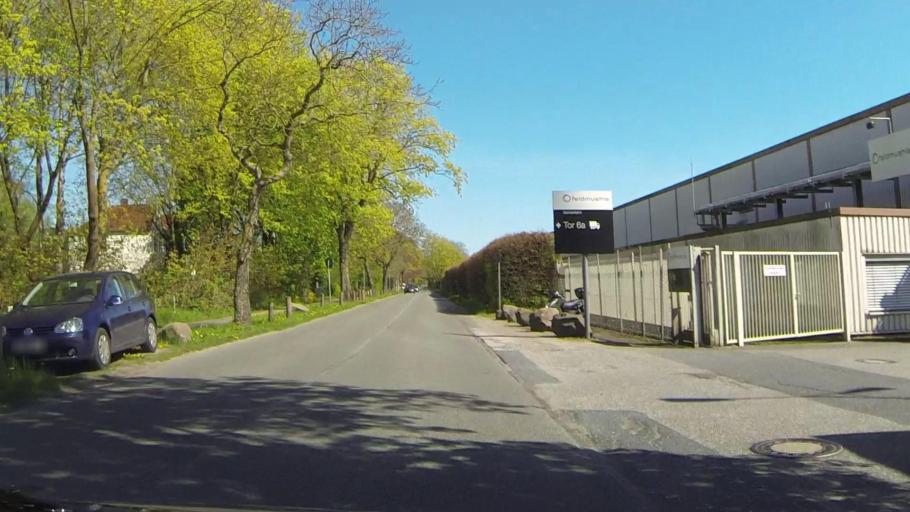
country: DE
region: Schleswig-Holstein
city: Uetersen
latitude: 53.6802
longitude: 9.6825
